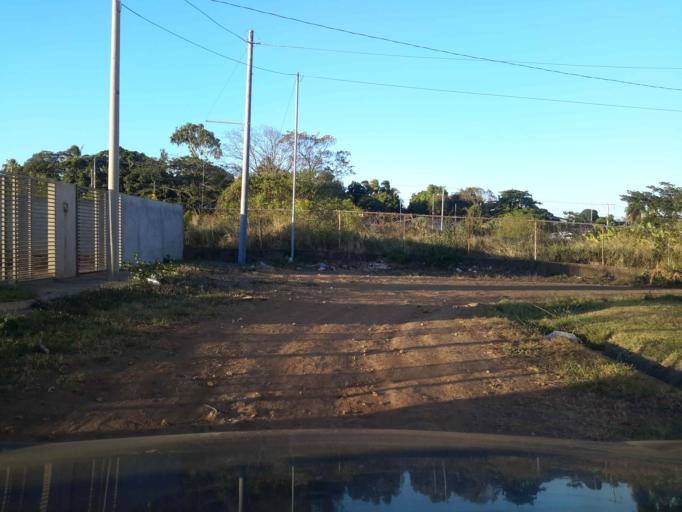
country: NI
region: Managua
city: Managua
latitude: 12.0928
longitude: -86.2262
